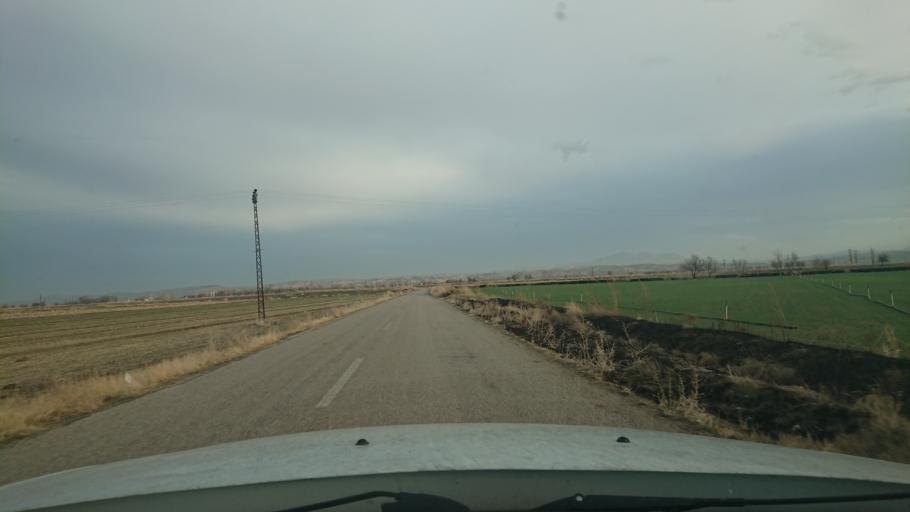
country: TR
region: Aksaray
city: Yesilova
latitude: 38.4329
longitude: 33.8367
